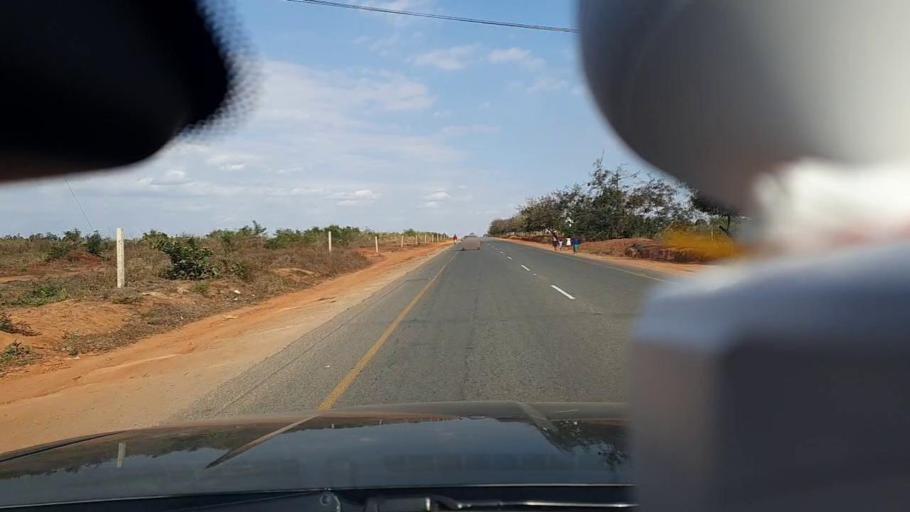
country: MZ
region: Nampula
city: Nampula
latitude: -15.1509
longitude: 39.3011
